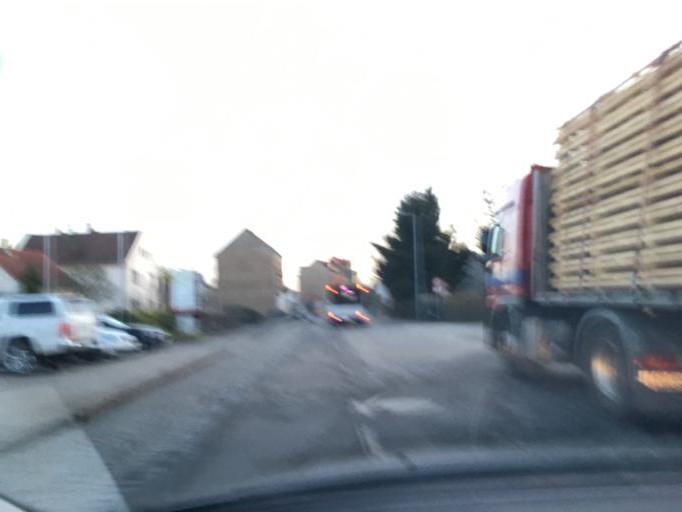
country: DE
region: Saxony
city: Taucha
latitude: 51.3353
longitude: 12.4846
